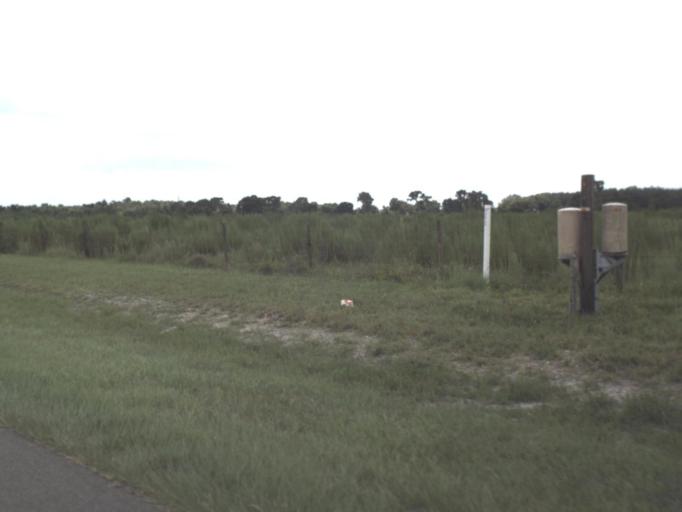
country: US
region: Florida
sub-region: Hillsborough County
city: Wimauma
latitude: 27.7113
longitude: -82.2715
